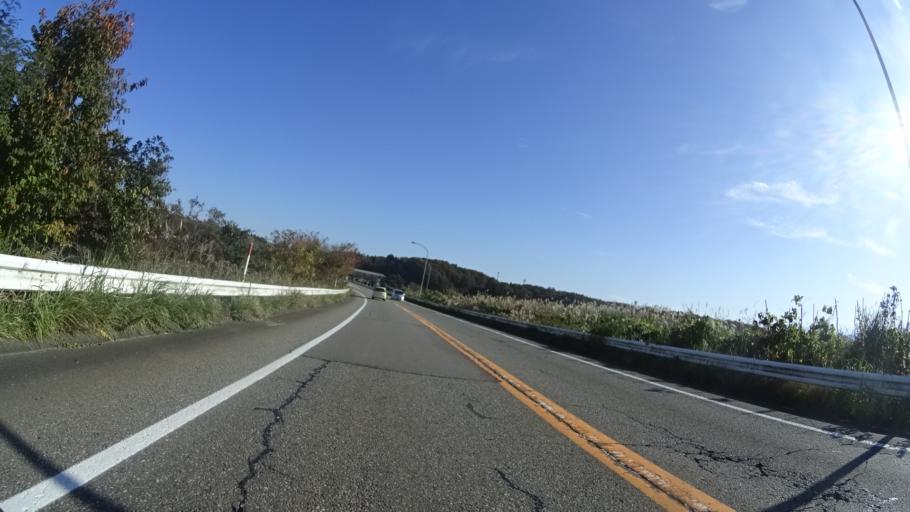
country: JP
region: Ishikawa
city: Komatsu
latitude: 36.3379
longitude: 136.4394
